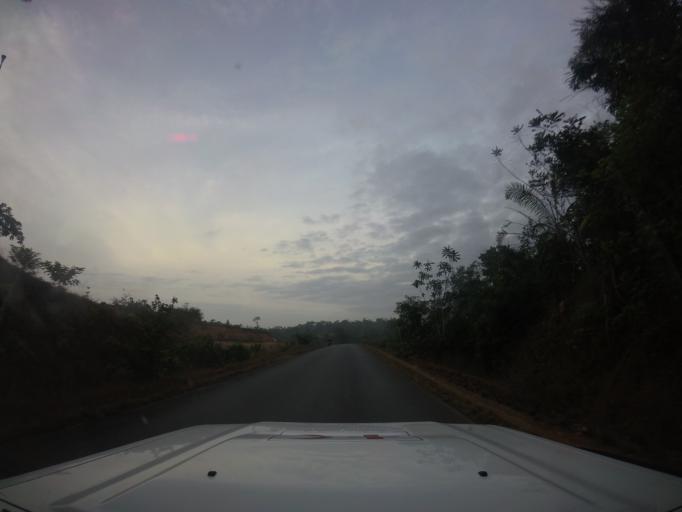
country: LR
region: Bomi
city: Tubmanburg
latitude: 6.7993
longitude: -10.8374
